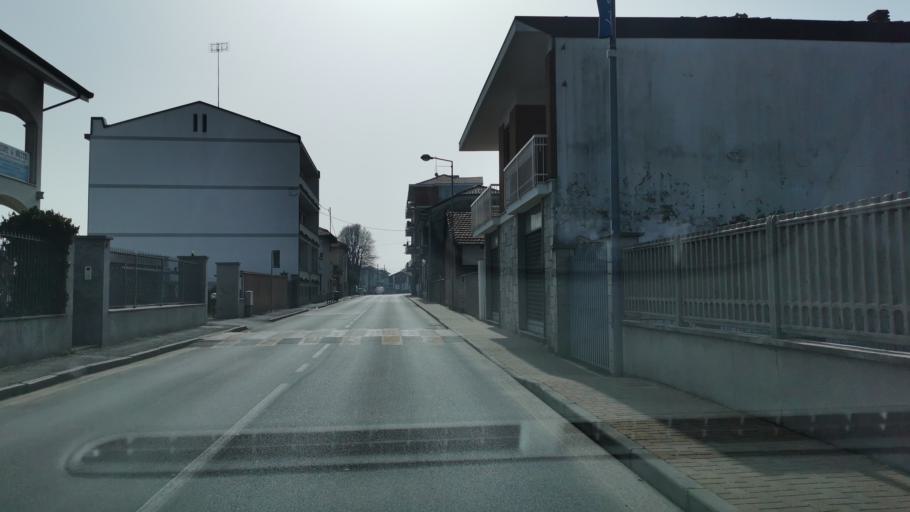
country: IT
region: Piedmont
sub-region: Provincia di Torino
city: Volpiano
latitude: 45.2026
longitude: 7.7796
